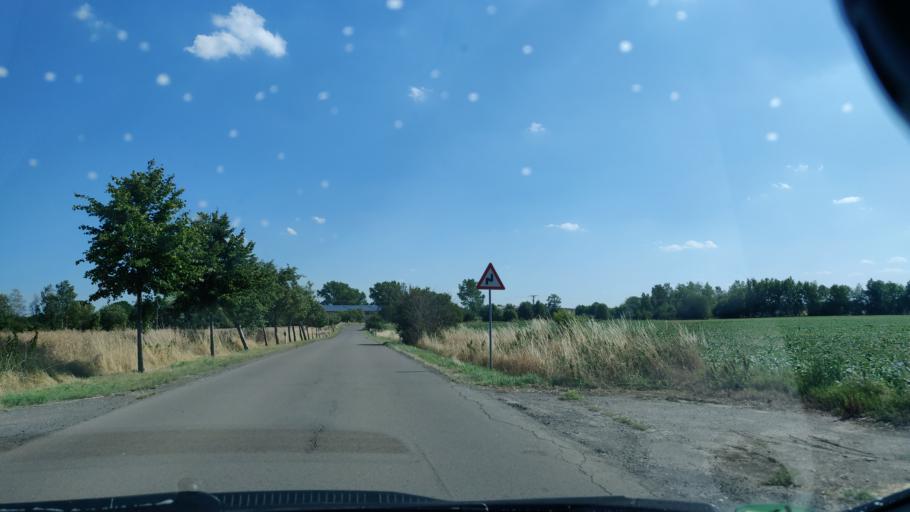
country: DE
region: Saxony
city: Borna
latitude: 51.0861
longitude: 12.5103
